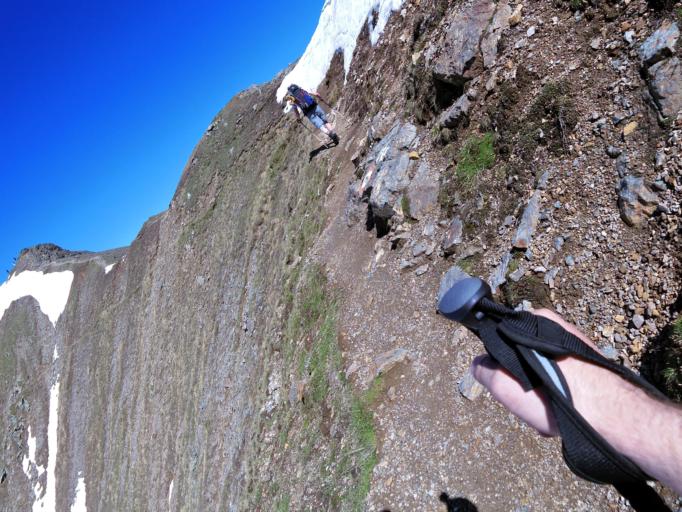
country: AT
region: Tyrol
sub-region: Politischer Bezirk Innsbruck Land
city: Neustift im Stubaital
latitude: 47.1447
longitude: 11.2679
